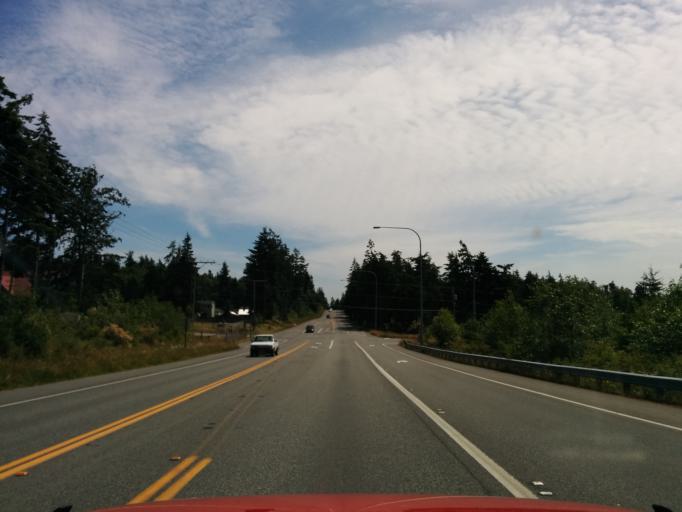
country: US
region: Washington
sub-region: Island County
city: Ault Field
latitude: 48.3701
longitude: -122.6539
